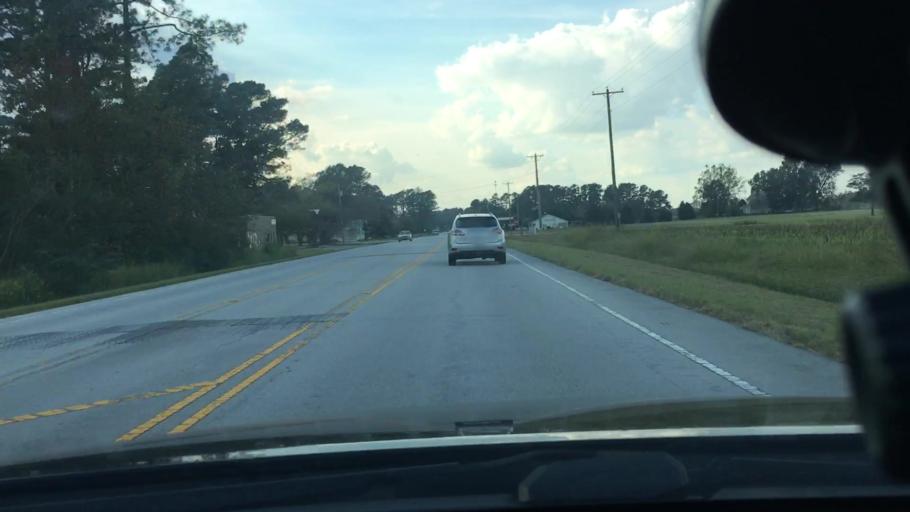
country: US
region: North Carolina
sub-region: Craven County
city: Vanceboro
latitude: 35.3770
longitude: -77.2156
